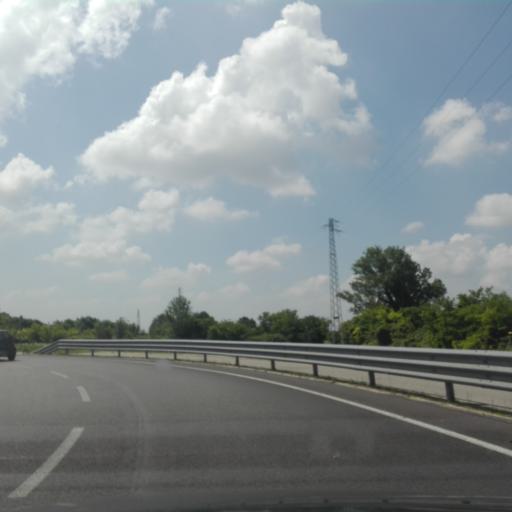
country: IT
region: Veneto
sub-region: Provincia di Rovigo
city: Rovigo
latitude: 45.0745
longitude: 11.8113
